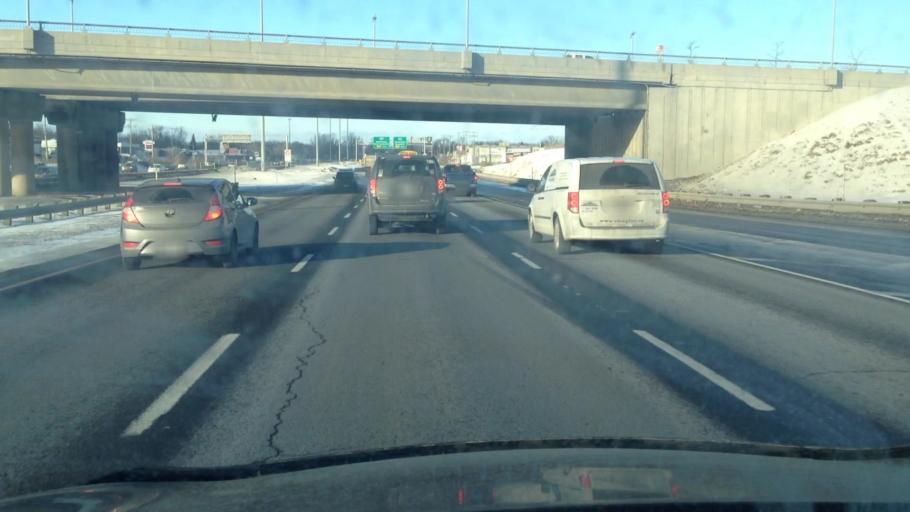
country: CA
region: Quebec
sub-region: Laurentides
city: Boisbriand
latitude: 45.5995
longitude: -73.8042
